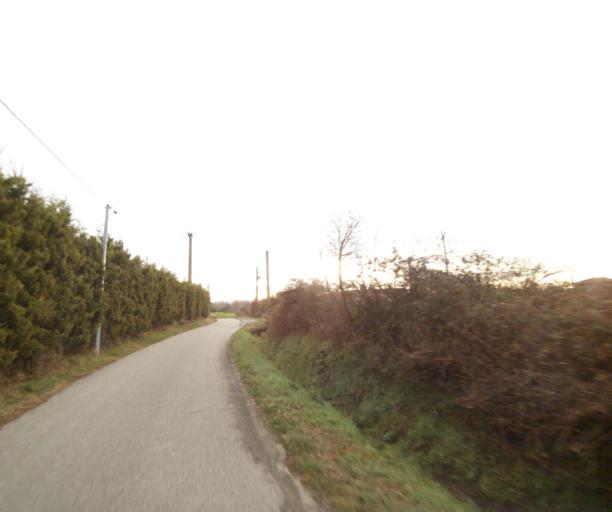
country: FR
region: Rhone-Alpes
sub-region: Departement de la Loire
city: Sury-le-Comtal
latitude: 45.5435
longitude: 4.1688
